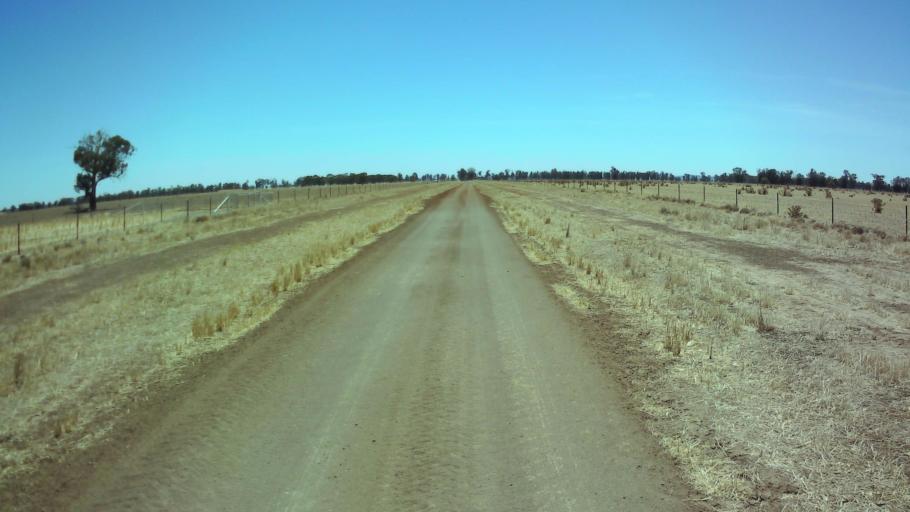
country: AU
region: New South Wales
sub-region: Weddin
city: Grenfell
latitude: -33.9844
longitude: 147.7354
